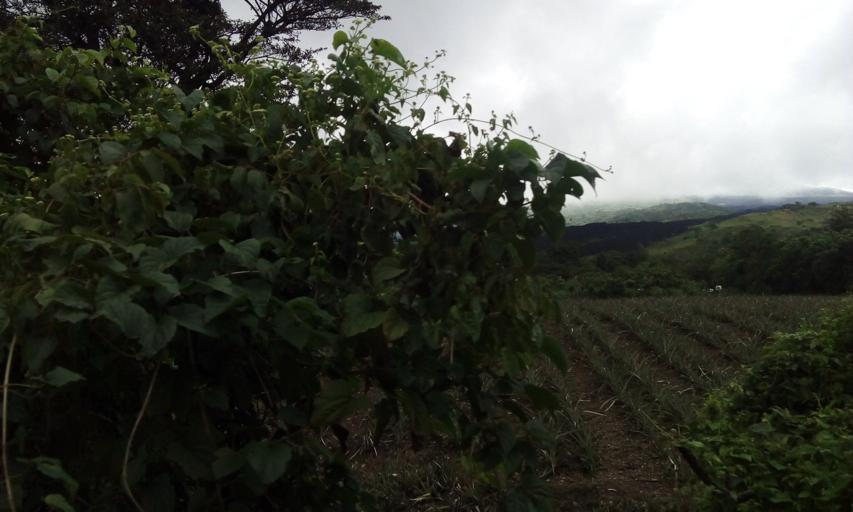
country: GT
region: Escuintla
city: San Vicente Pacaya
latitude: 14.3357
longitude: -90.6112
